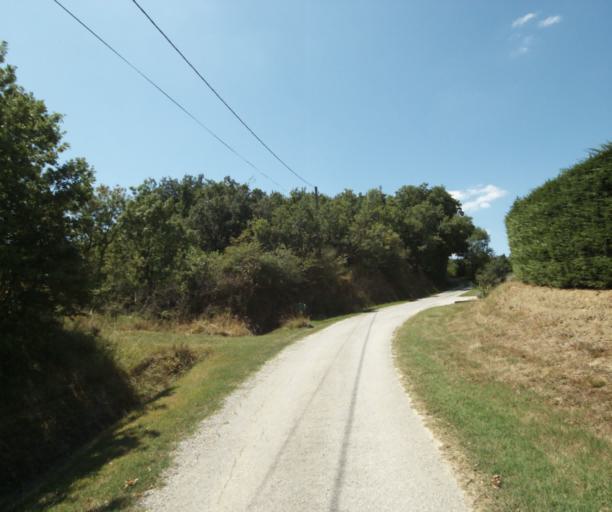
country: FR
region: Midi-Pyrenees
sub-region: Departement de la Haute-Garonne
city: Saint-Felix-Lauragais
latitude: 43.4847
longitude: 1.8684
